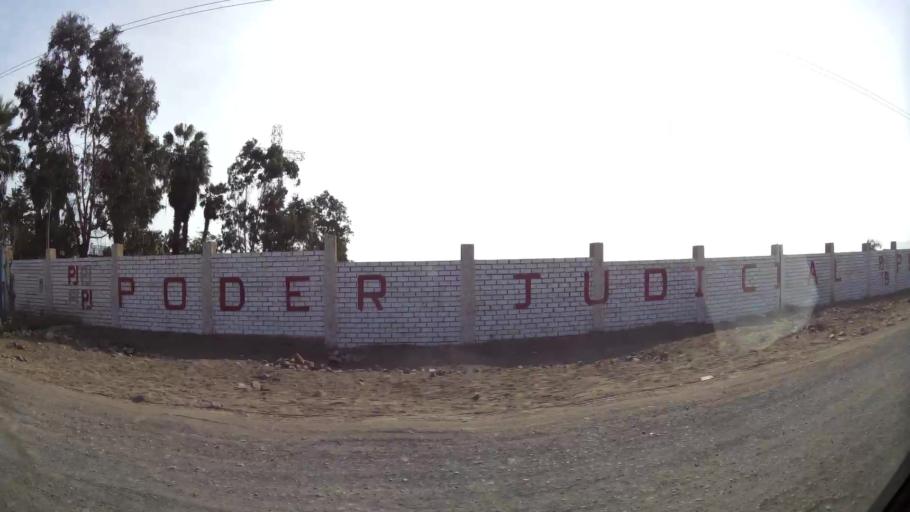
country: PE
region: Lima
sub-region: Lima
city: Santa Rosa
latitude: -11.7545
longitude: -77.1693
